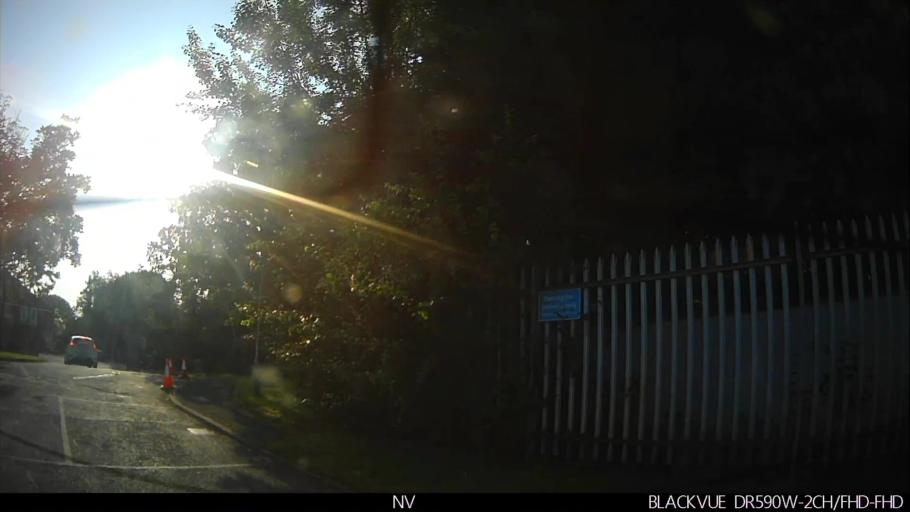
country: GB
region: England
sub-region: City of York
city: Wigginton
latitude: 54.0195
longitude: -1.0819
